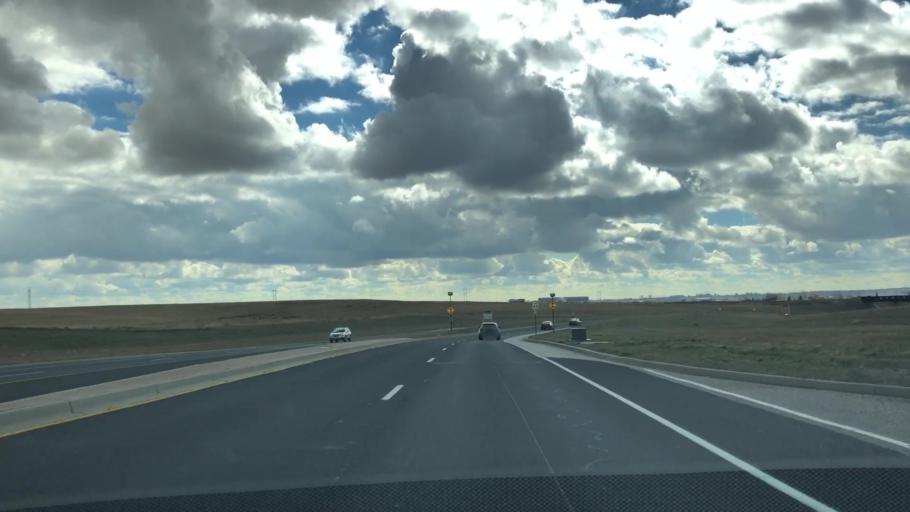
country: US
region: Colorado
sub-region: Larimer County
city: Loveland
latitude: 40.4203
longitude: -104.9838
